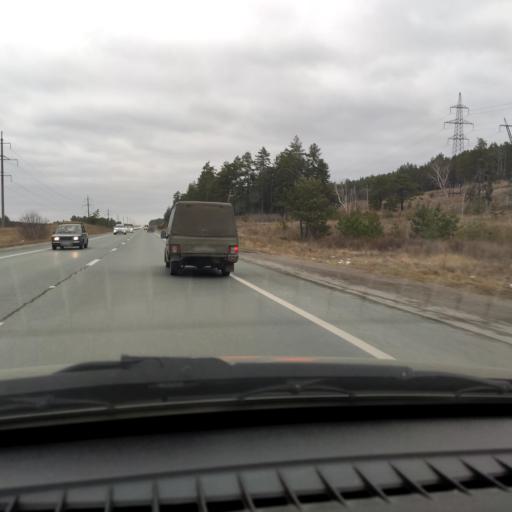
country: RU
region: Samara
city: Volzhskiy
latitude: 53.4494
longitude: 50.0953
